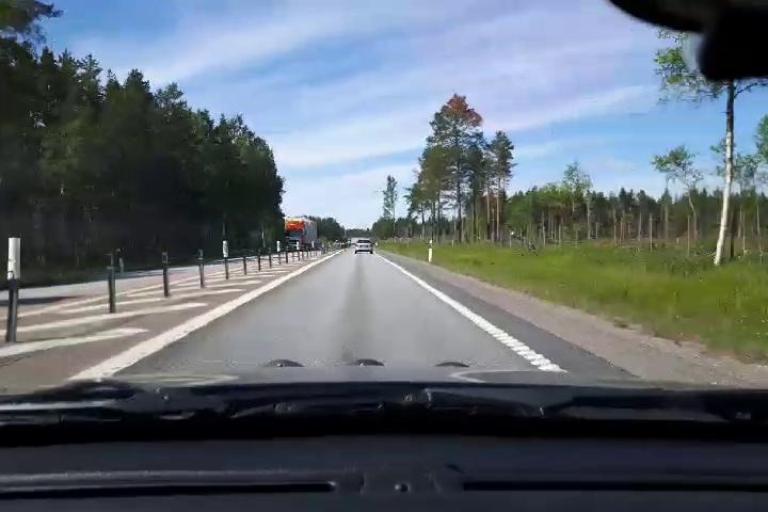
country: SE
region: Gaevleborg
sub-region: Gavle Kommun
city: Norrsundet
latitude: 60.9731
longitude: 17.0230
